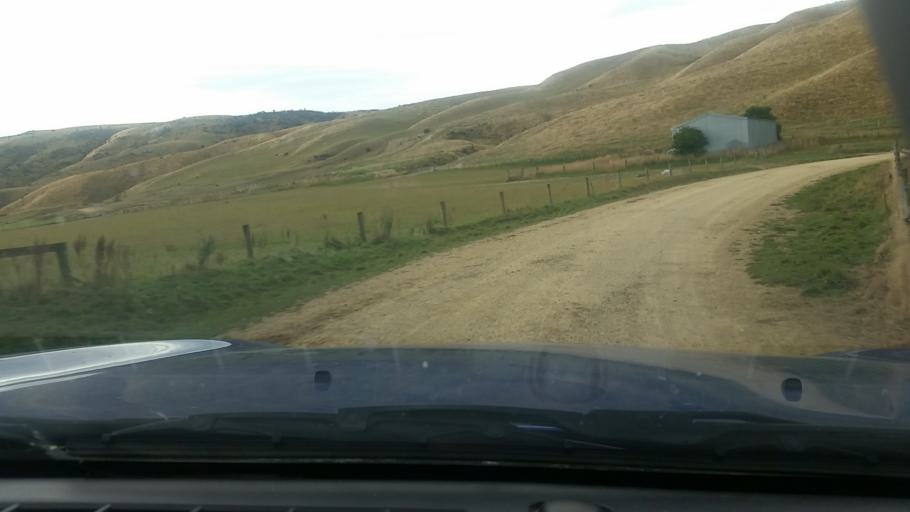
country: NZ
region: Otago
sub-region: Clutha District
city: Balclutha
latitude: -45.7229
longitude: 169.5420
